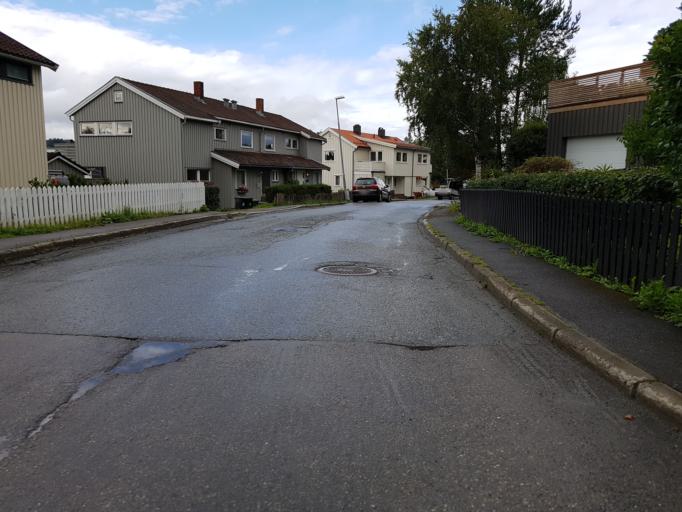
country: NO
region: Sor-Trondelag
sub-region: Trondheim
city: Trondheim
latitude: 63.3991
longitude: 10.4120
